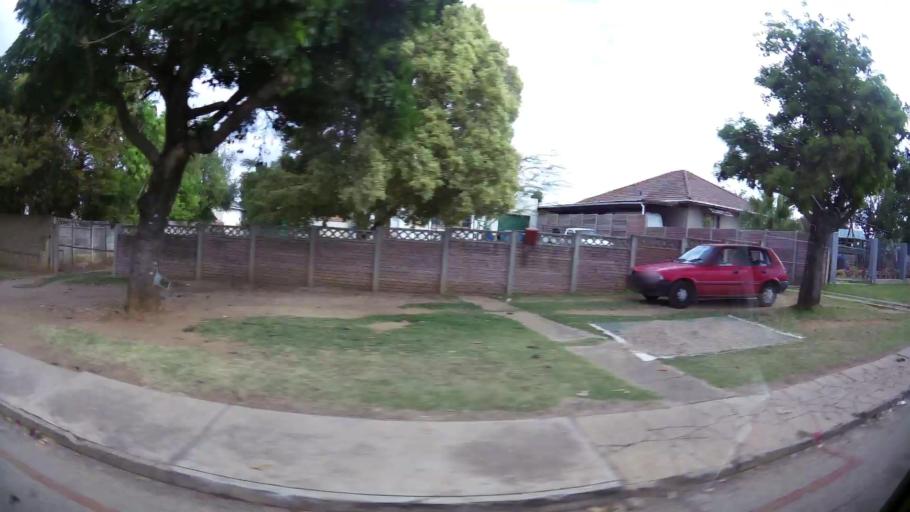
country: ZA
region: Eastern Cape
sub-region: Nelson Mandela Bay Metropolitan Municipality
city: Uitenhage
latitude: -33.7503
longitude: 25.4071
